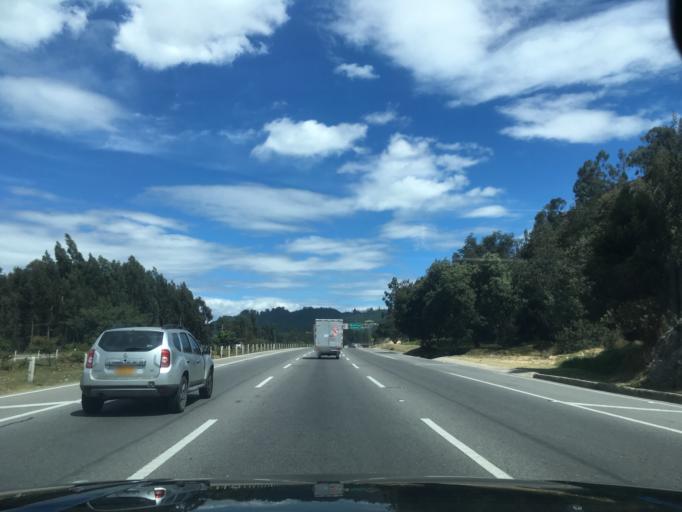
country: CO
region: Cundinamarca
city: Cajica
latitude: 4.9274
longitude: -73.9950
